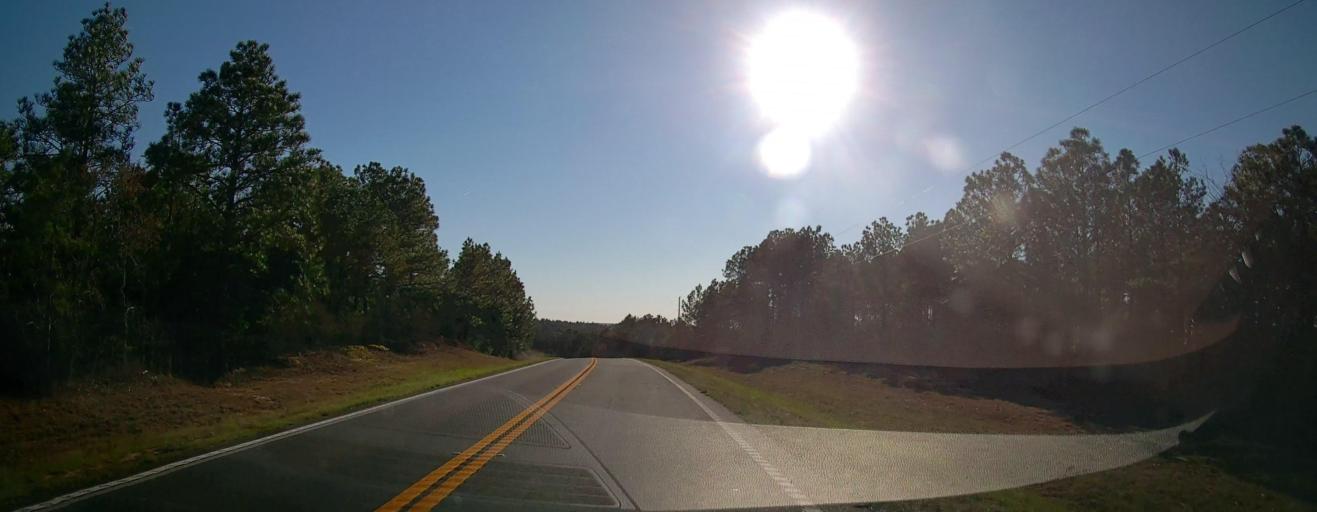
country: US
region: Georgia
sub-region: Taylor County
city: Butler
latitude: 32.5495
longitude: -84.2778
